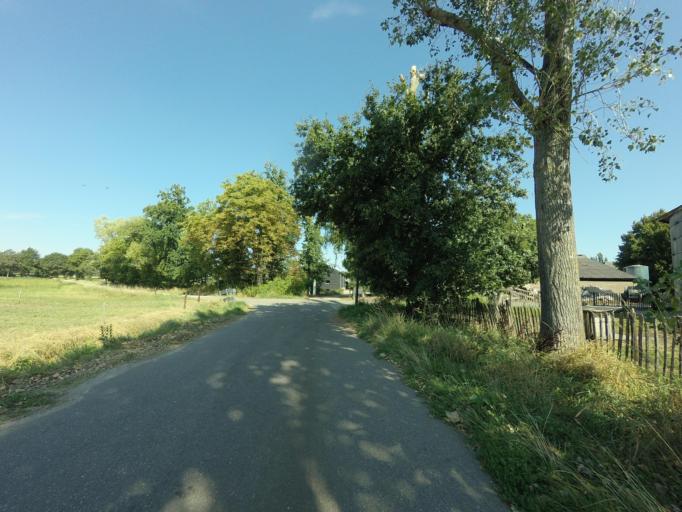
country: NL
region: North Brabant
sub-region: Gemeente Waalre
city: Waalre
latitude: 51.3870
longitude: 5.4287
